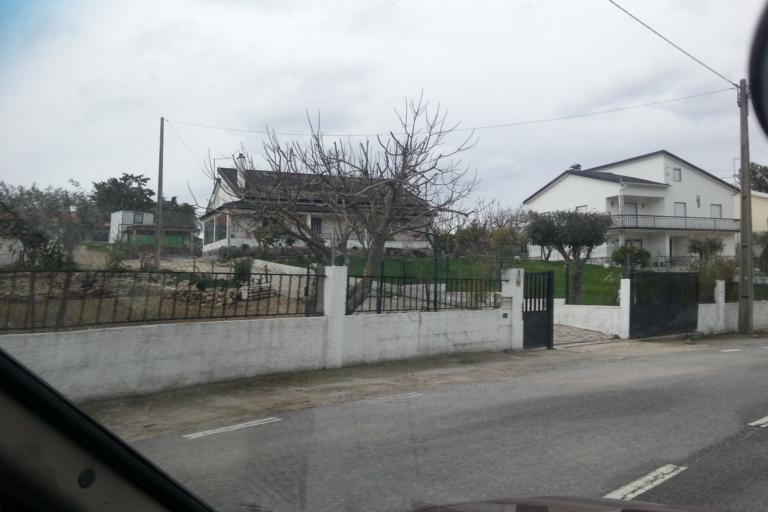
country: PT
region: Guarda
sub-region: Fornos de Algodres
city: Fornos de Algodres
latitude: 40.5259
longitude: -7.5793
